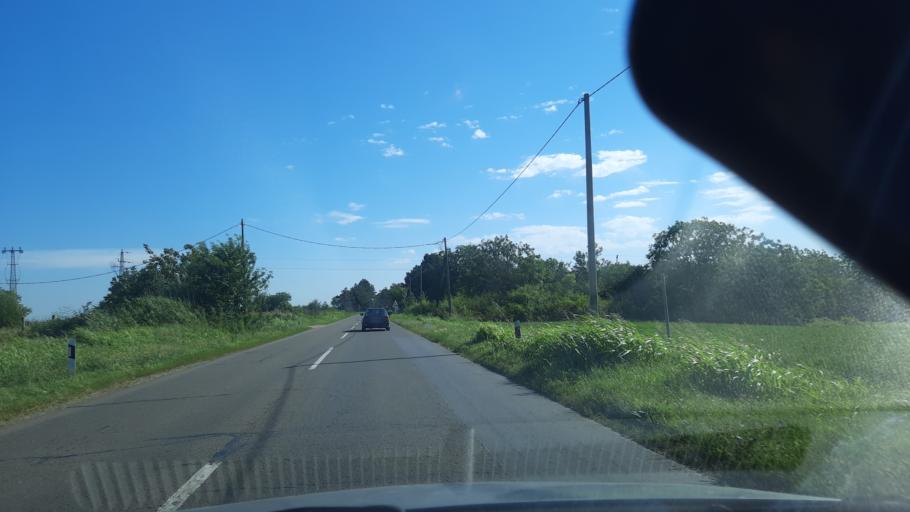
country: RS
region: Autonomna Pokrajina Vojvodina
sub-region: Juznobanatski Okrug
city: Kovin
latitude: 44.7651
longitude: 20.9886
